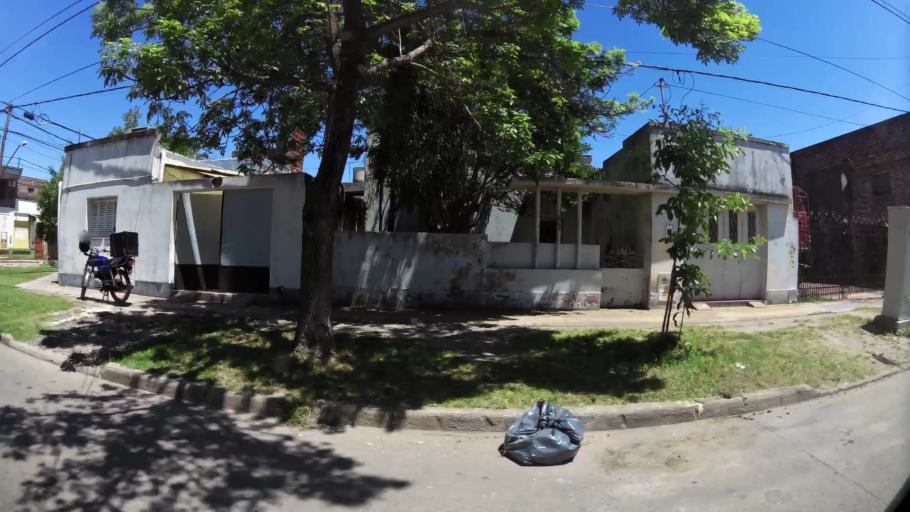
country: AR
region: Santa Fe
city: Santa Fe de la Vera Cruz
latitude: -31.6266
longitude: -60.7118
